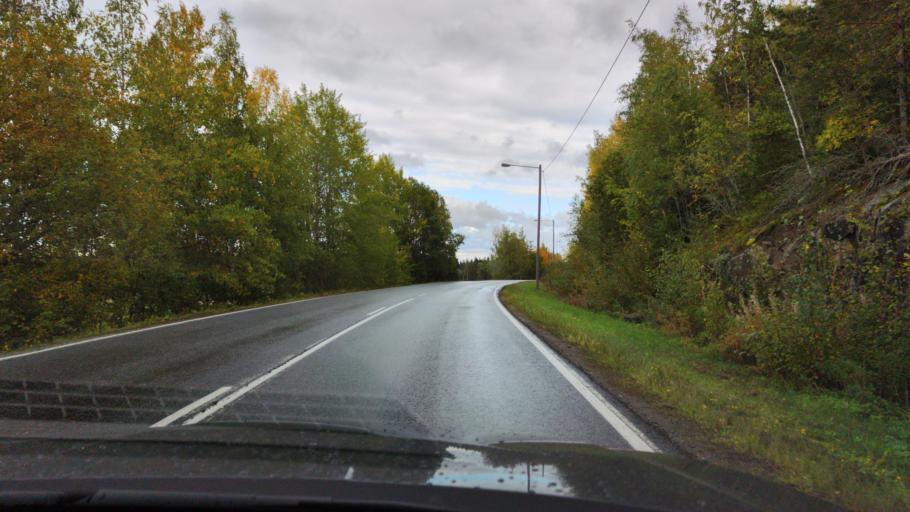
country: FI
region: Varsinais-Suomi
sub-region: Turku
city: Turku
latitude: 60.3655
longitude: 22.2034
